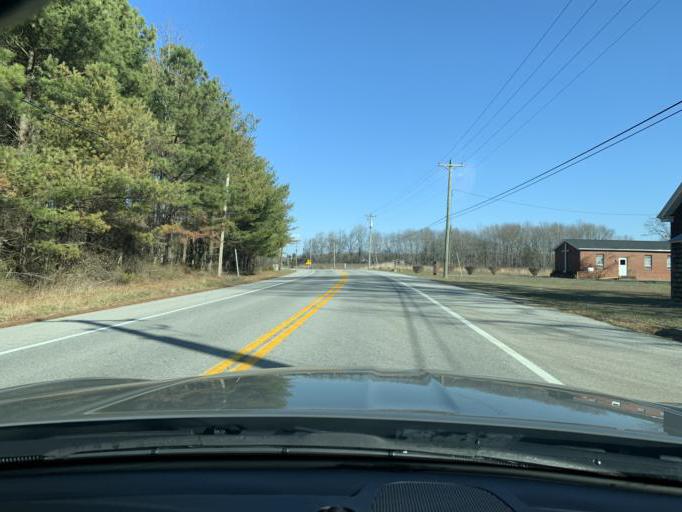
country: US
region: Maryland
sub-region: Queen Anne's County
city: Centreville
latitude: 39.1177
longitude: -76.0184
